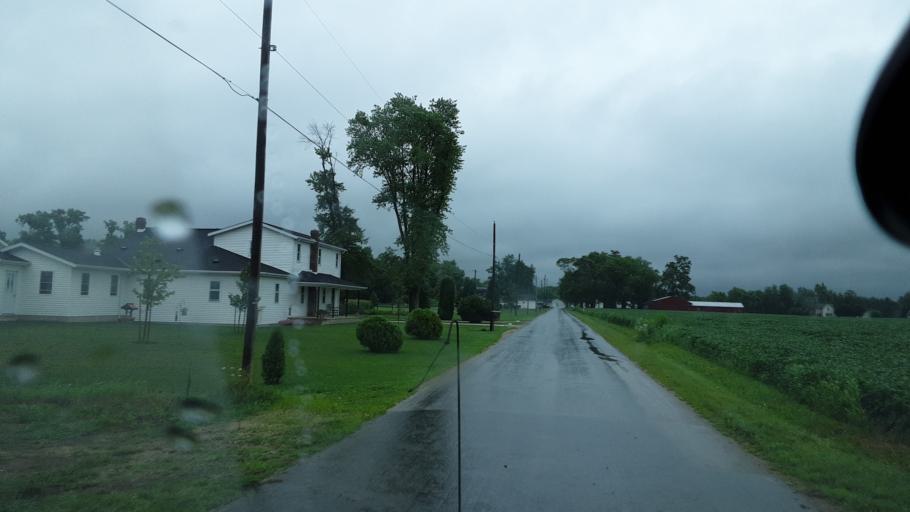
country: US
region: Indiana
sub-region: Adams County
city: Decatur
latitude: 40.7757
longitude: -84.8463
